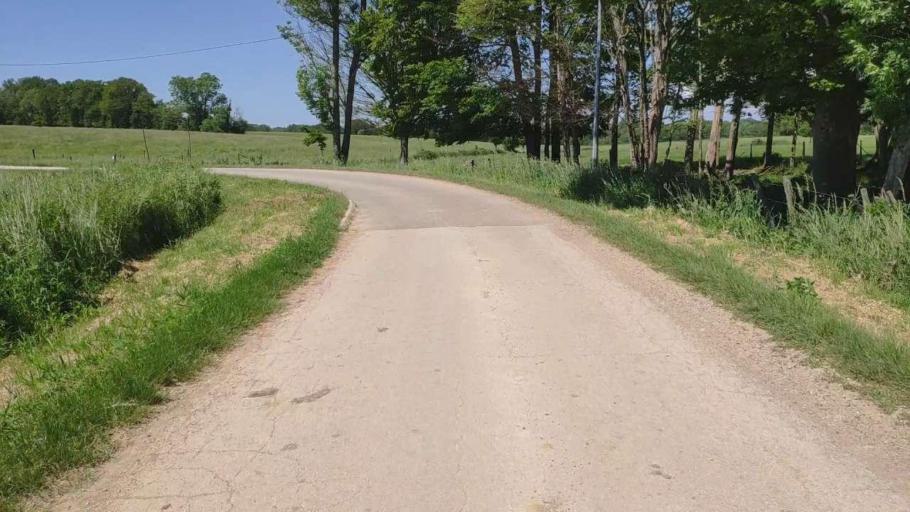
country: FR
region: Franche-Comte
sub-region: Departement du Jura
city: Bletterans
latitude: 46.7751
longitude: 5.3924
